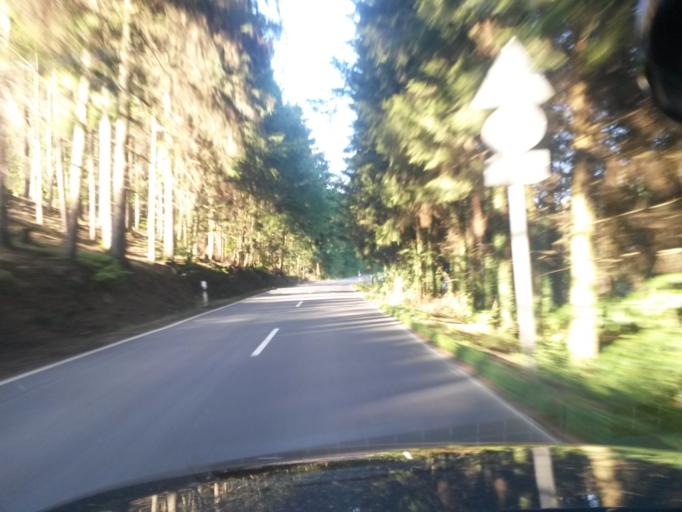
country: DE
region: North Rhine-Westphalia
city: Wiehl
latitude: 50.9677
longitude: 7.5814
